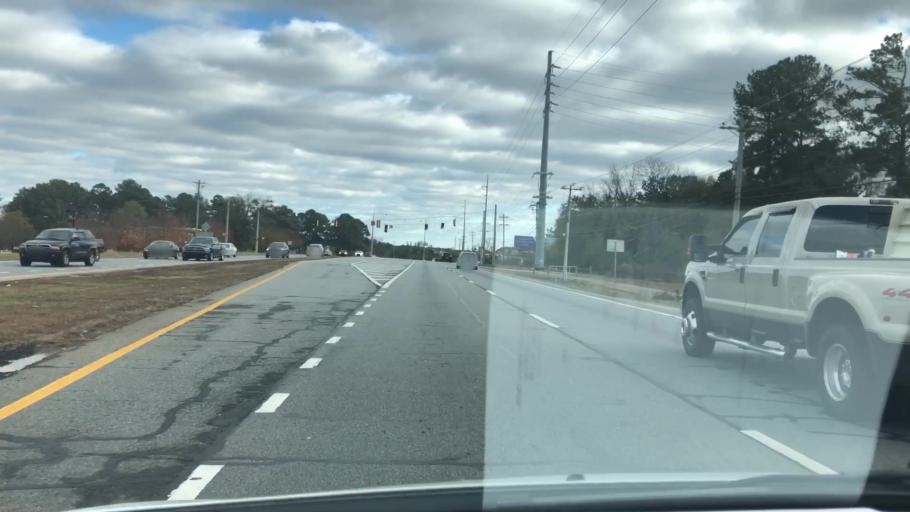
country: US
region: Georgia
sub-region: Fulton County
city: Johns Creek
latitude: 34.0944
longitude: -84.1755
